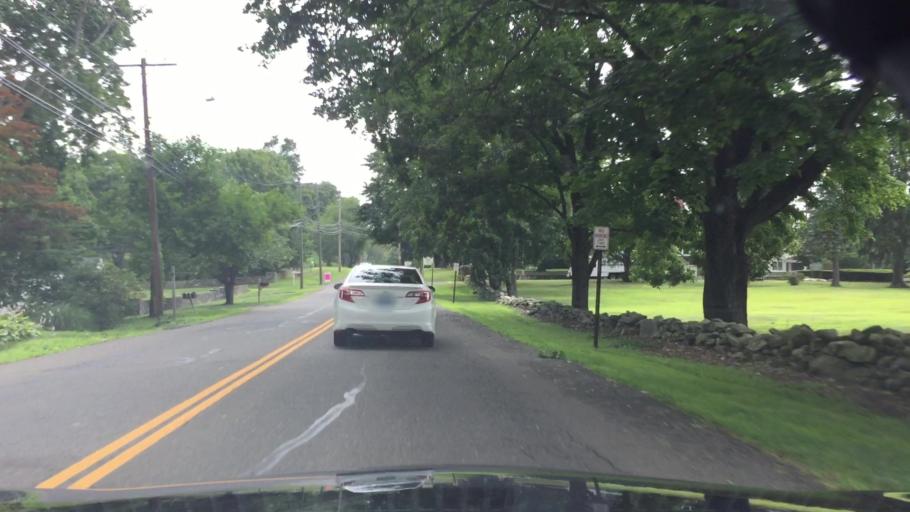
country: US
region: Connecticut
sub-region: New Haven County
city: City of Milford (balance)
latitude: 41.2342
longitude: -73.1124
